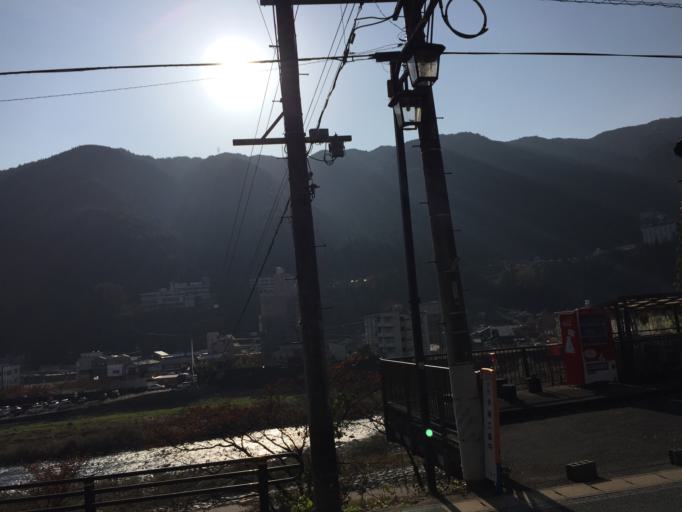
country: JP
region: Gifu
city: Gujo
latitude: 35.8096
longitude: 137.2408
